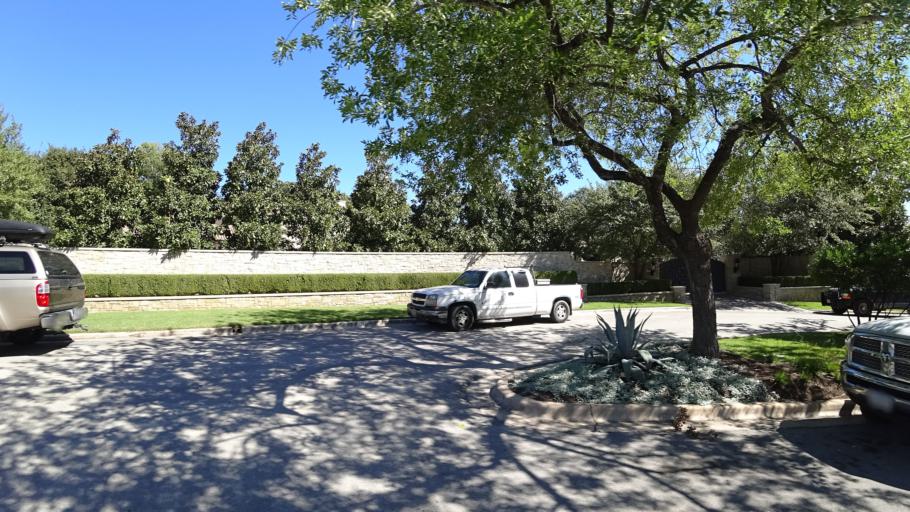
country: US
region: Texas
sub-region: Travis County
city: West Lake Hills
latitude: 30.3160
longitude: -97.7689
